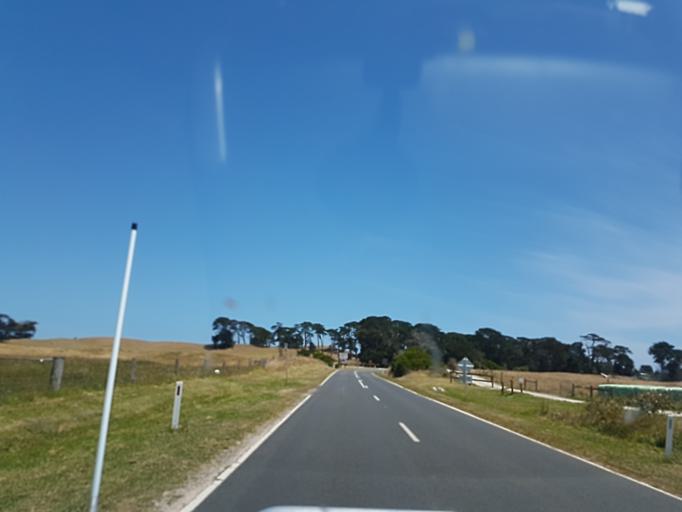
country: AU
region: Victoria
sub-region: Bass Coast
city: North Wonthaggi
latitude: -38.7011
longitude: 145.8361
